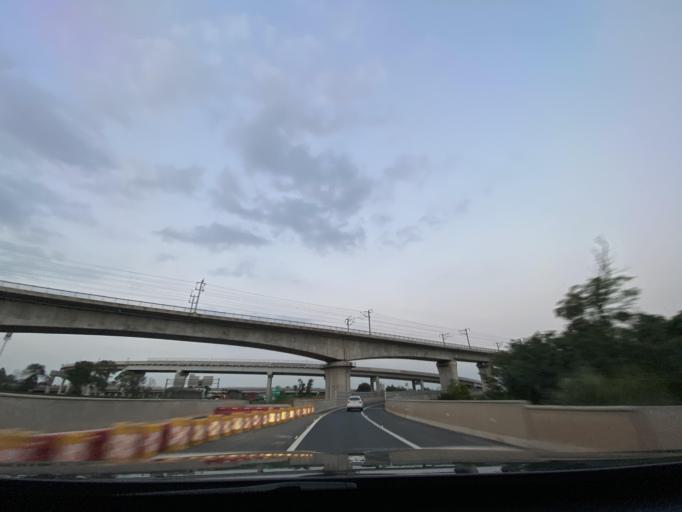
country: CN
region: Sichuan
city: Chengdu
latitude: 30.5718
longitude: 104.1349
